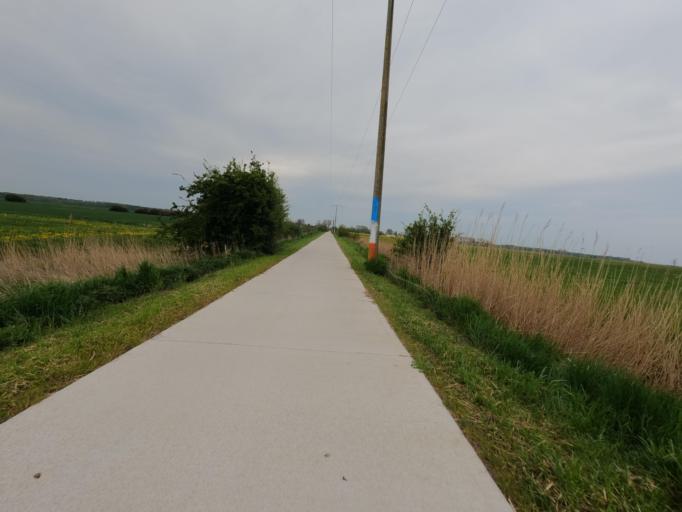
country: DE
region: Mecklenburg-Vorpommern
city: Saal
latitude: 54.3041
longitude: 12.4988
